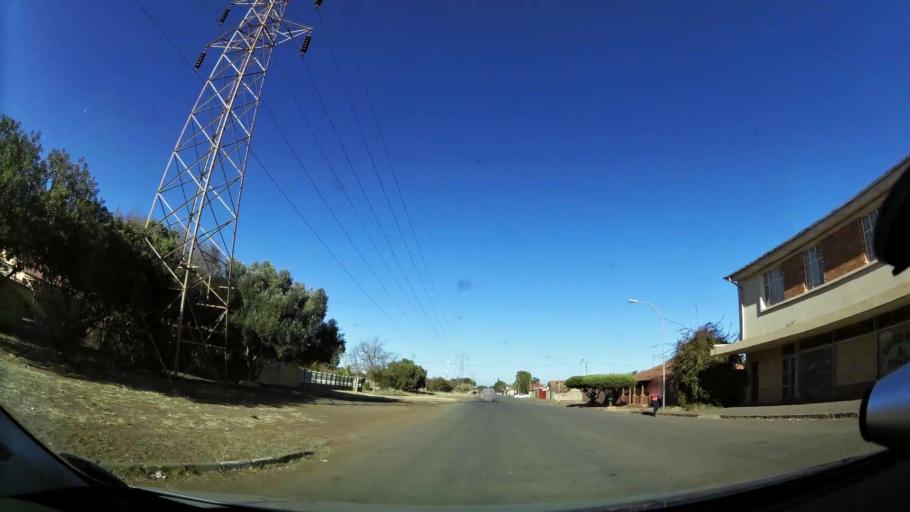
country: ZA
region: Northern Cape
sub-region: Frances Baard District Municipality
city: Kimberley
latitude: -28.7594
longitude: 24.7847
